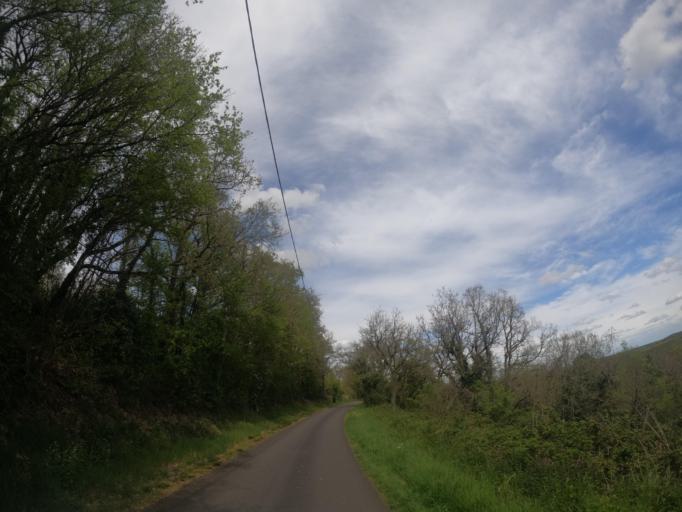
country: FR
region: Poitou-Charentes
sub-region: Departement des Deux-Sevres
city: Saint-Jean-de-Thouars
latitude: 46.9249
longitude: -0.1928
